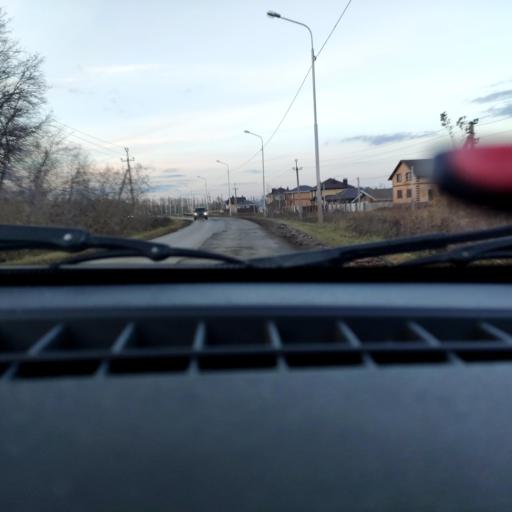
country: RU
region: Bashkortostan
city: Ufa
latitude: 54.6614
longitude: 55.9179
